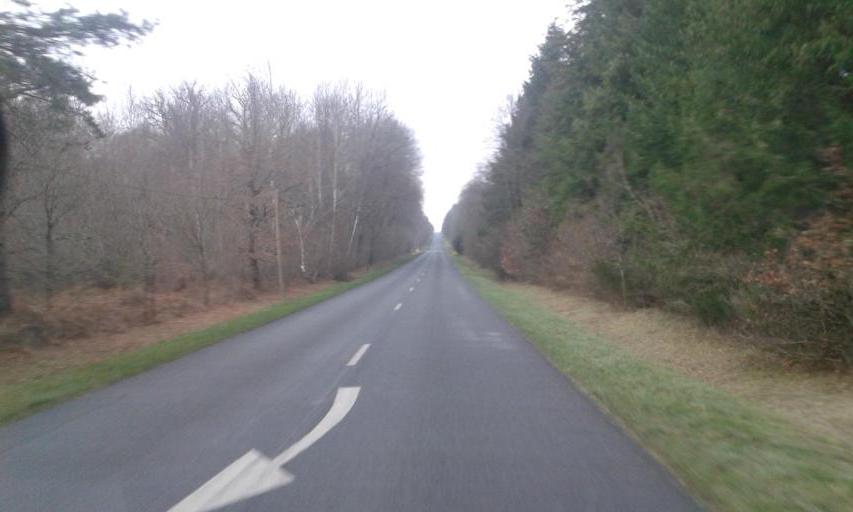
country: FR
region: Centre
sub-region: Departement du Loir-et-Cher
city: Dhuizon
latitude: 47.6323
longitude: 1.6642
